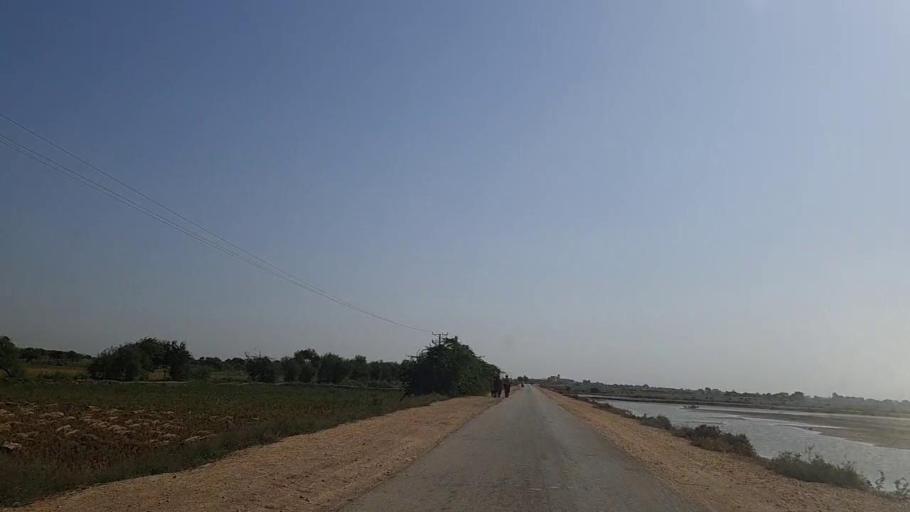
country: PK
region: Sindh
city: Mirpur Batoro
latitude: 24.6275
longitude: 68.2939
